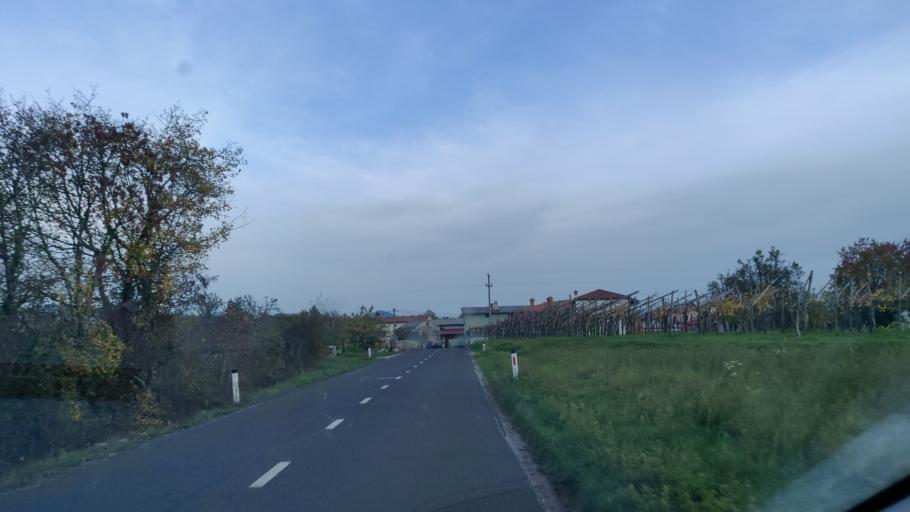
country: SI
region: Sezana
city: Sezana
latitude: 45.7621
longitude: 13.9036
